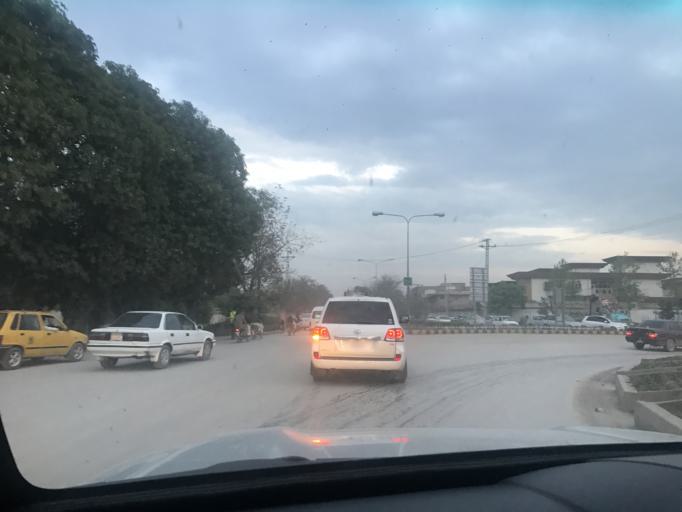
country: PK
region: Khyber Pakhtunkhwa
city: Peshawar
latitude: 33.9780
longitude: 71.4465
